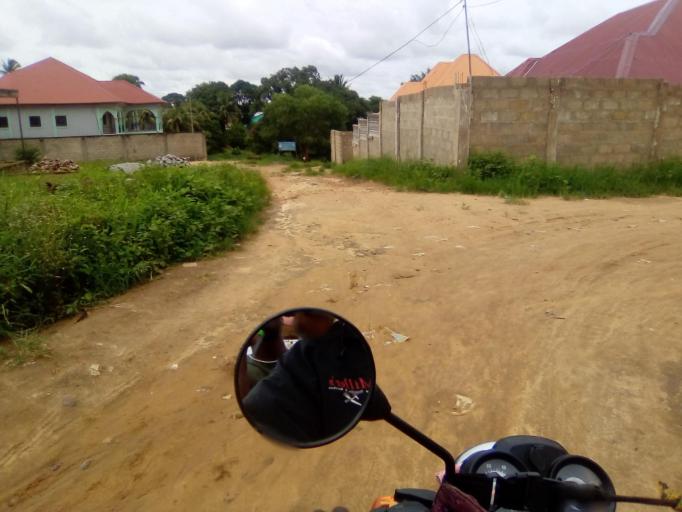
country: SL
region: Southern Province
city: Bo
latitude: 7.9399
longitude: -11.7302
